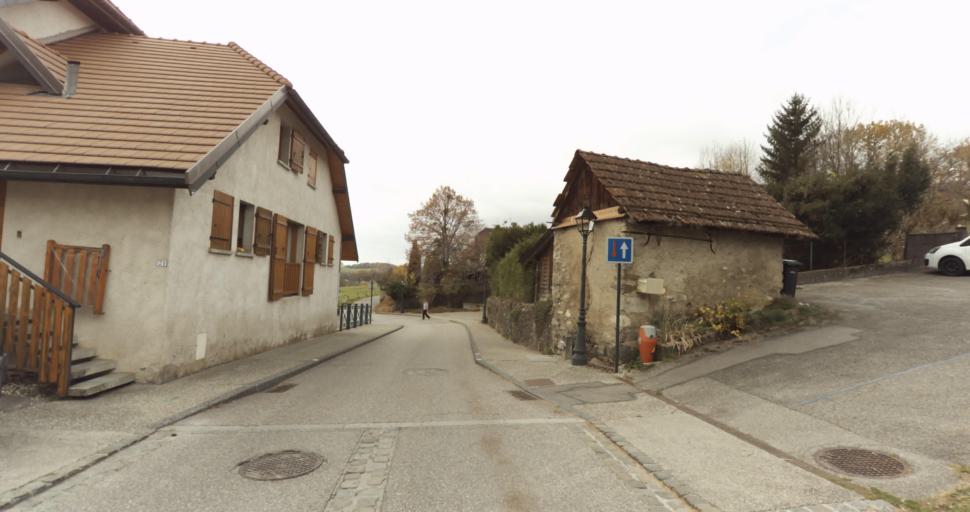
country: FR
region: Rhone-Alpes
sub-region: Departement de la Haute-Savoie
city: Pringy
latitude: 45.9537
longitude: 6.1115
